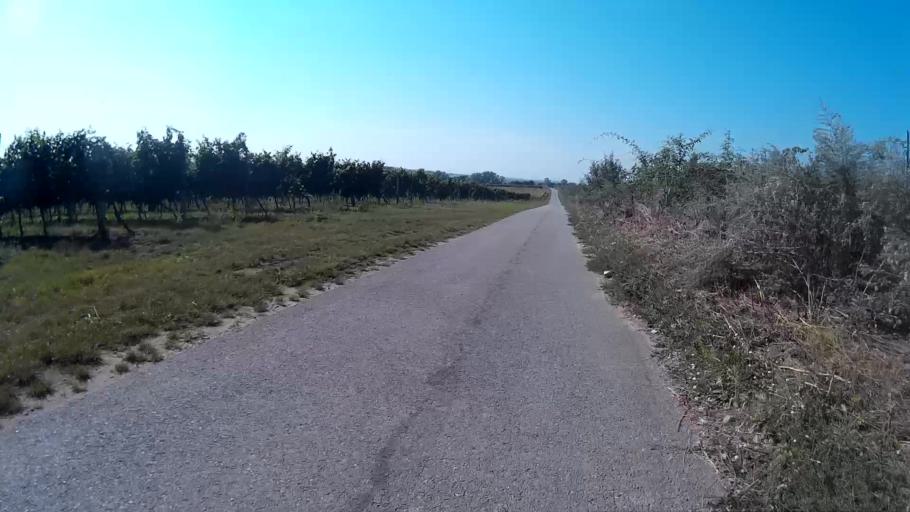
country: CZ
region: South Moravian
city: Novosedly
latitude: 48.8428
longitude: 16.5221
